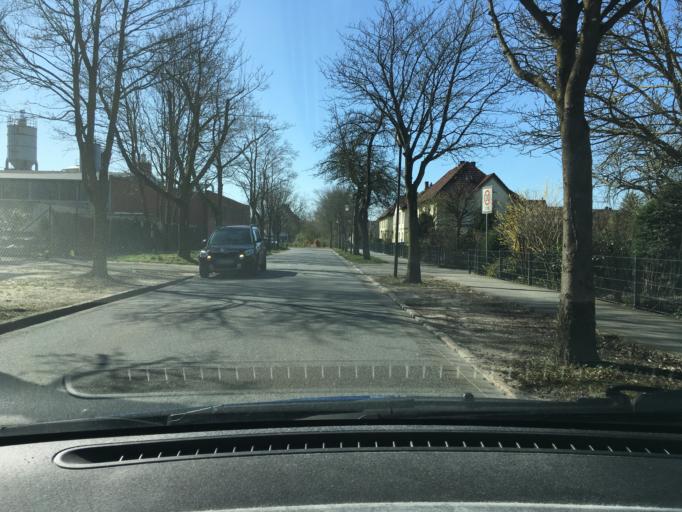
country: DE
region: Lower Saxony
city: Uelzen
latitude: 52.9721
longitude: 10.5489
